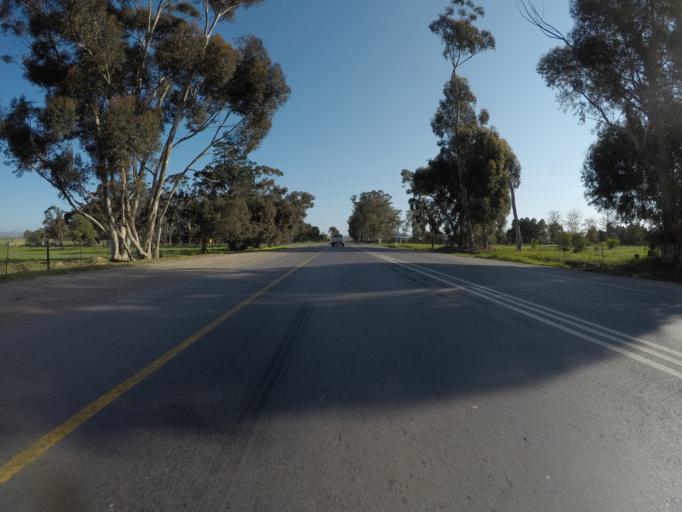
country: ZA
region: Western Cape
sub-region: City of Cape Town
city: Kraaifontein
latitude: -33.7932
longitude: 18.6954
